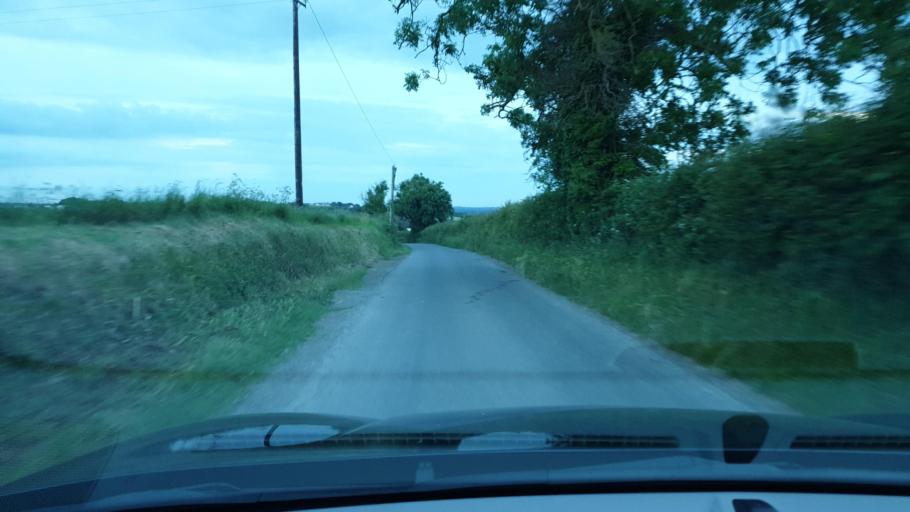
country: IE
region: Leinster
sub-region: An Mhi
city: Duleek
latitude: 53.6053
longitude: -6.3643
